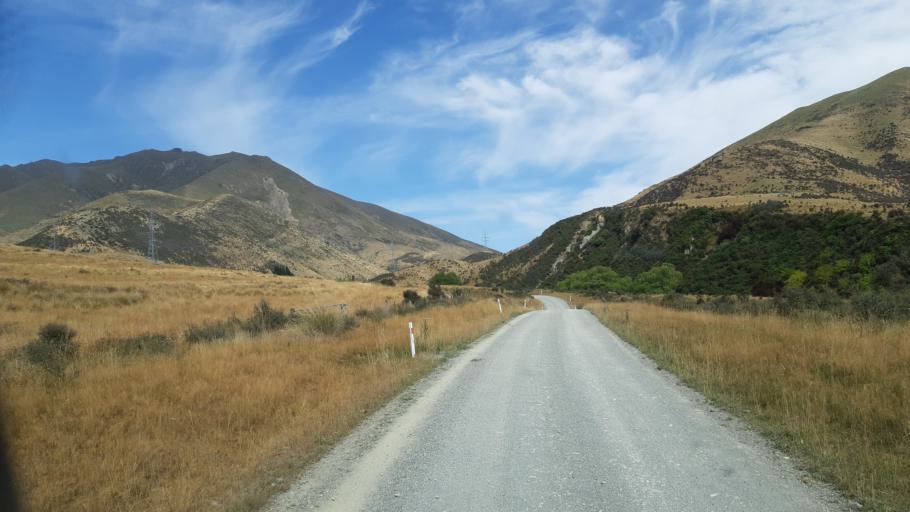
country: NZ
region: Canterbury
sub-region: Timaru District
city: Pleasant Point
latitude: -44.1897
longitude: 170.6514
